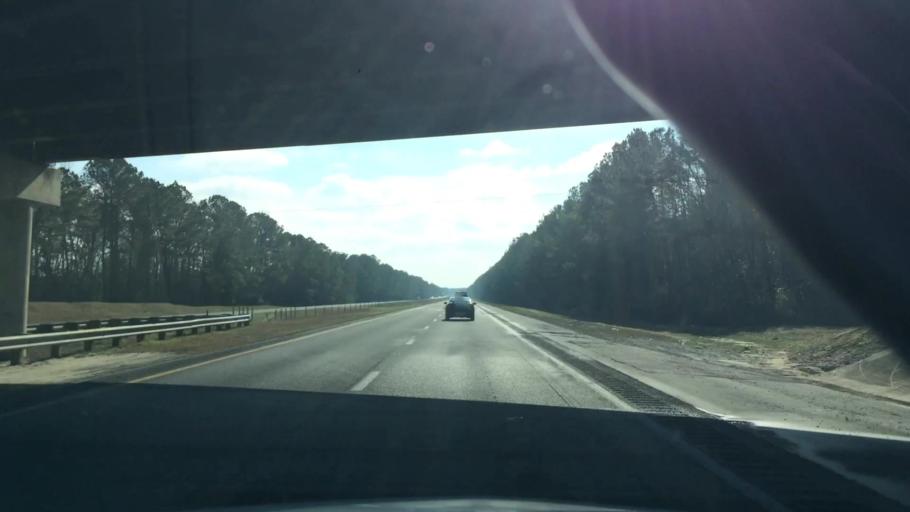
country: US
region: North Carolina
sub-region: Duplin County
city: Wallace
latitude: 34.7320
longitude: -77.9449
